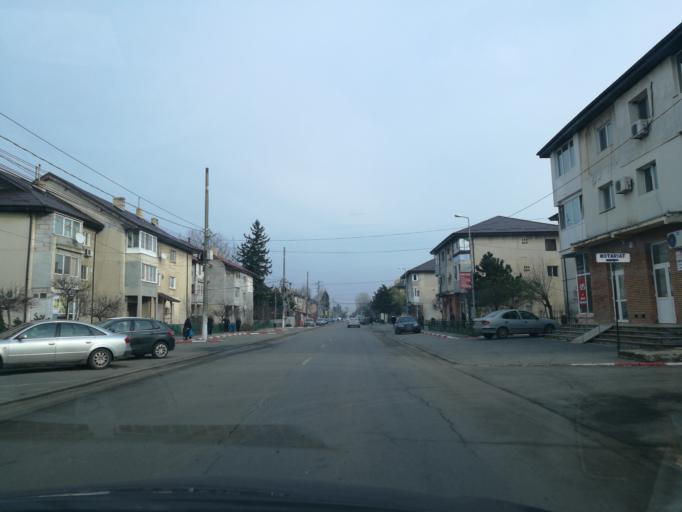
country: RO
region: Ilfov
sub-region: Comuna Corbeanca
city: Corbeanca
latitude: 44.6110
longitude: 26.0754
